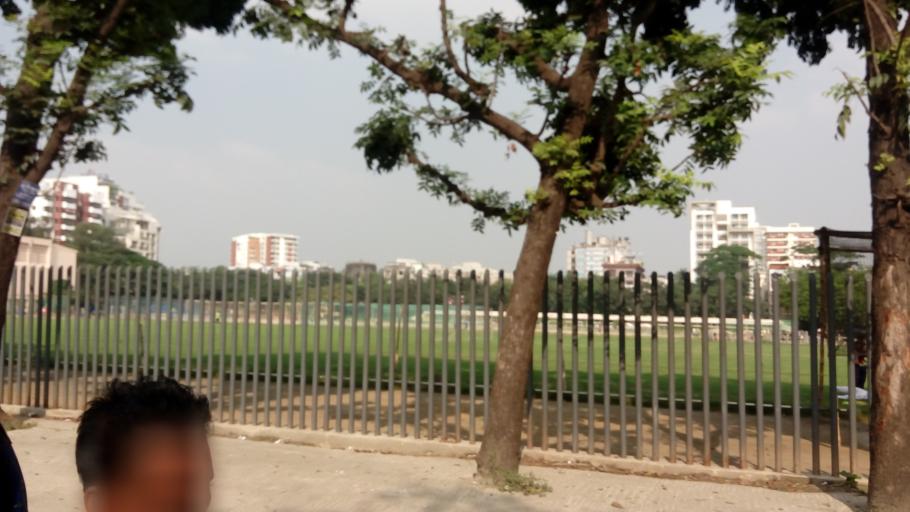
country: BD
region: Dhaka
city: Azimpur
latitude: 23.7481
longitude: 90.3702
